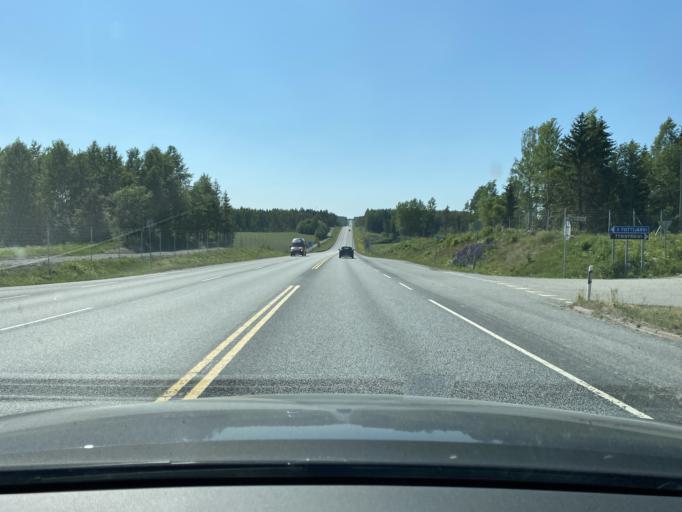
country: FI
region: Pirkanmaa
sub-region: Tampere
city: Nokia
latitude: 61.4055
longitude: 23.2842
